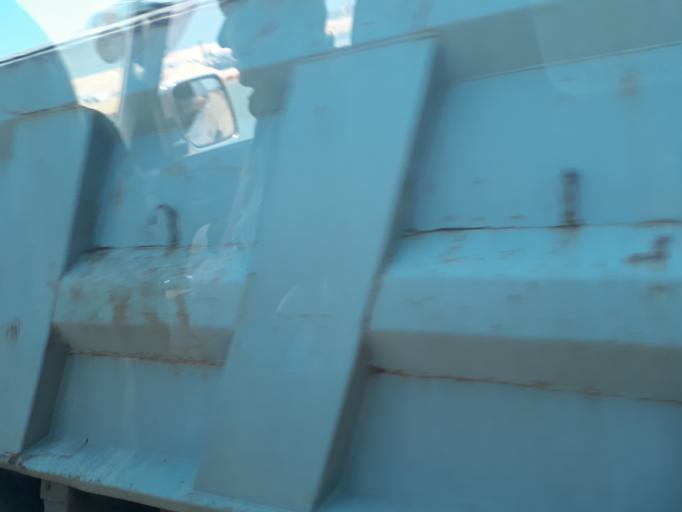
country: LK
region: Western
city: Colombo
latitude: 6.9247
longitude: 79.8377
